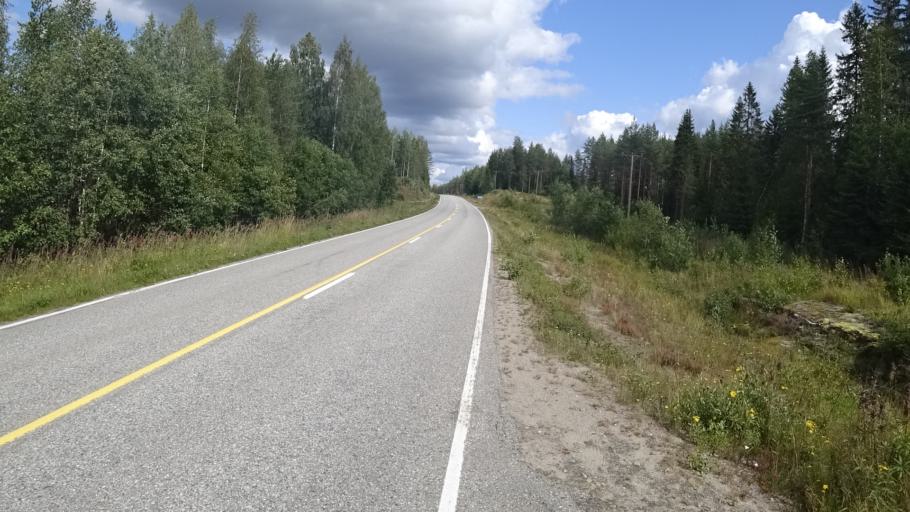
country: FI
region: North Karelia
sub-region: Joensuu
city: Ilomantsi
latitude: 62.6292
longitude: 31.2709
